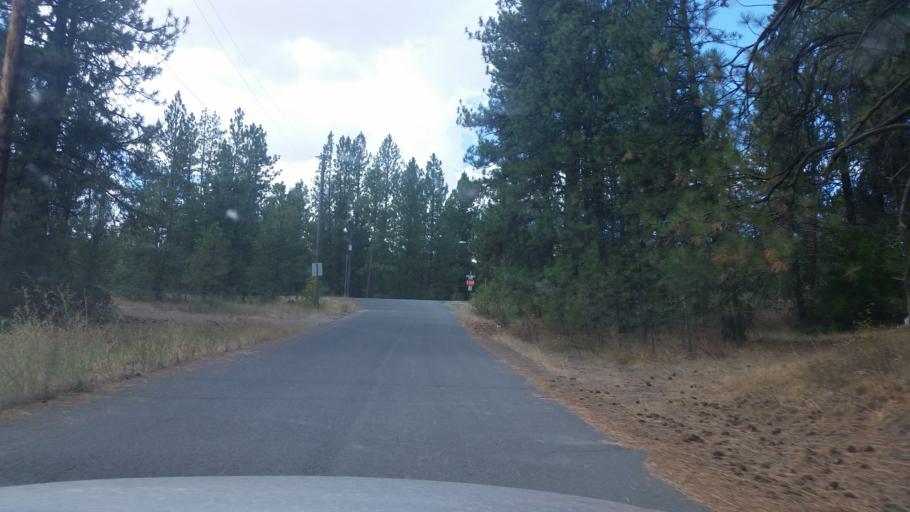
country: US
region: Washington
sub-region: Spokane County
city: Cheney
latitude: 47.5234
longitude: -117.5170
